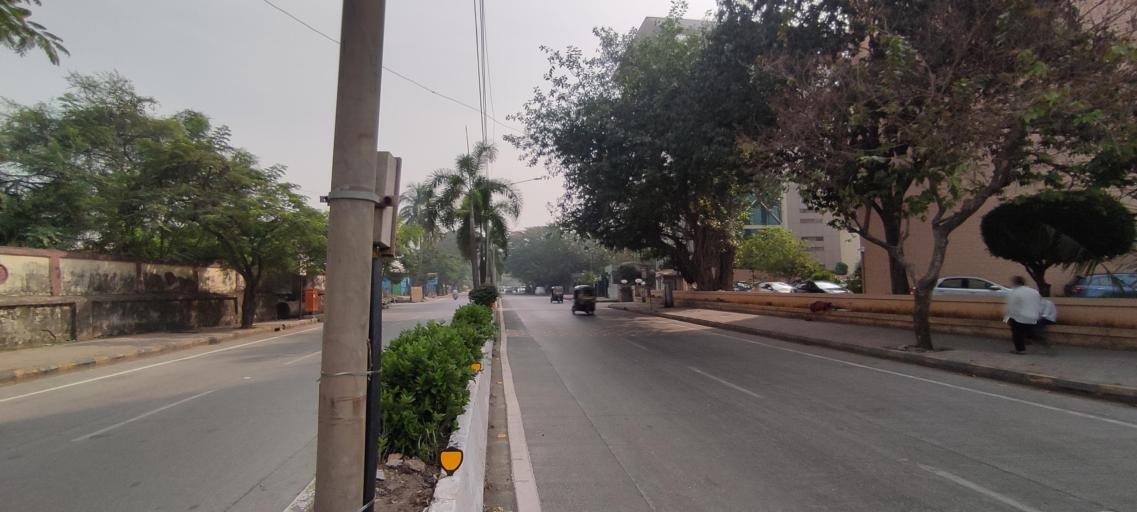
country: IN
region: Maharashtra
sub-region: Mumbai Suburban
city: Mumbai
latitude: 19.0661
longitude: 72.8597
